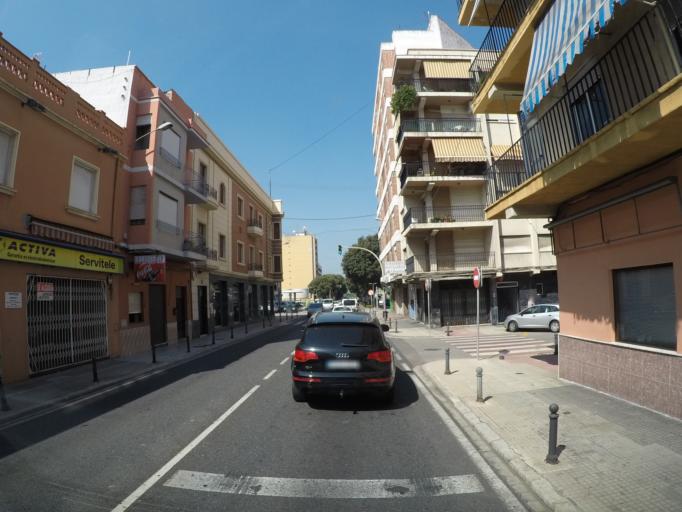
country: ES
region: Valencia
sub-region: Provincia de Valencia
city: Oliva
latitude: 38.9222
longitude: -0.1234
